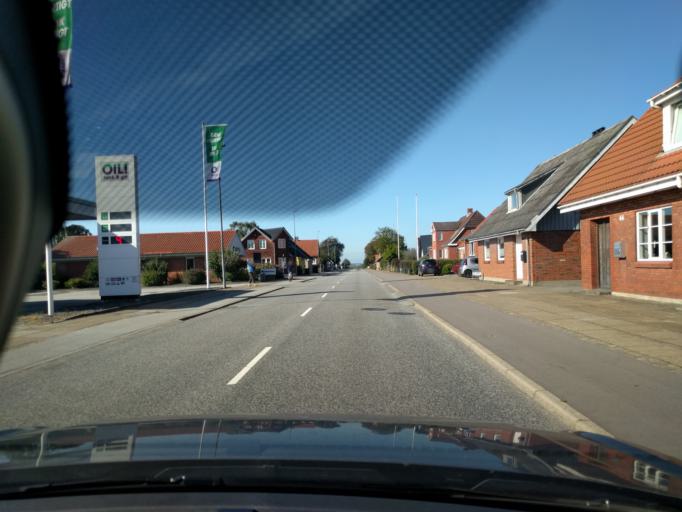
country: DK
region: North Denmark
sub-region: Vesthimmerland Kommune
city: Alestrup
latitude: 56.7080
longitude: 9.6282
